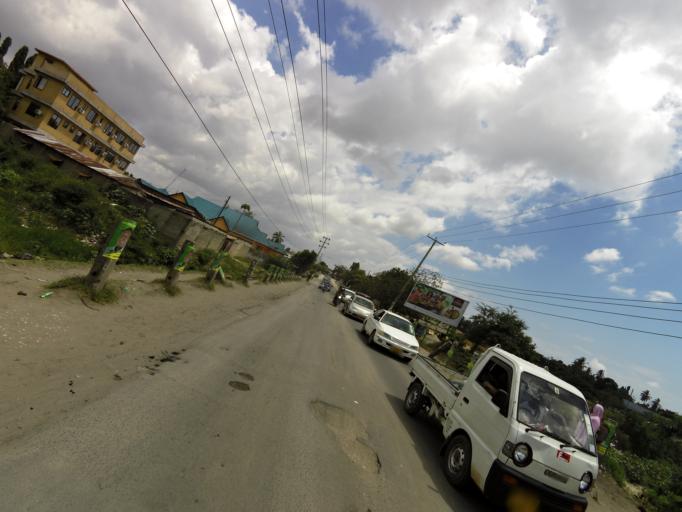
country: TZ
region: Dar es Salaam
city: Magomeni
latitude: -6.7895
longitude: 39.2309
